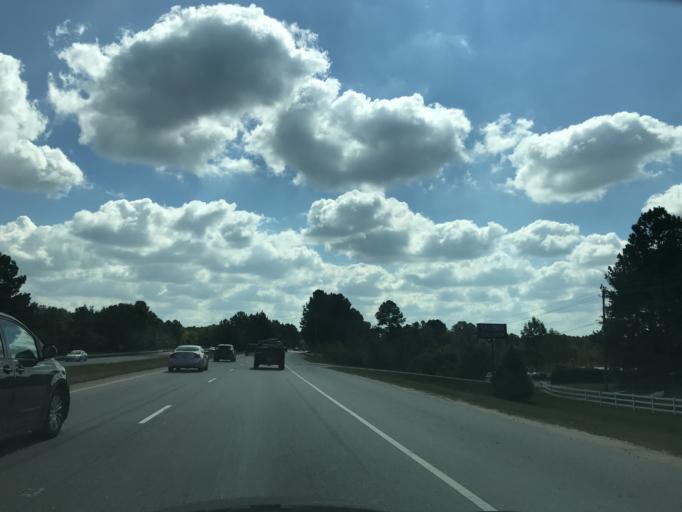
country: US
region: North Carolina
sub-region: Wake County
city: Wake Forest
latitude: 35.9277
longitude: -78.5433
